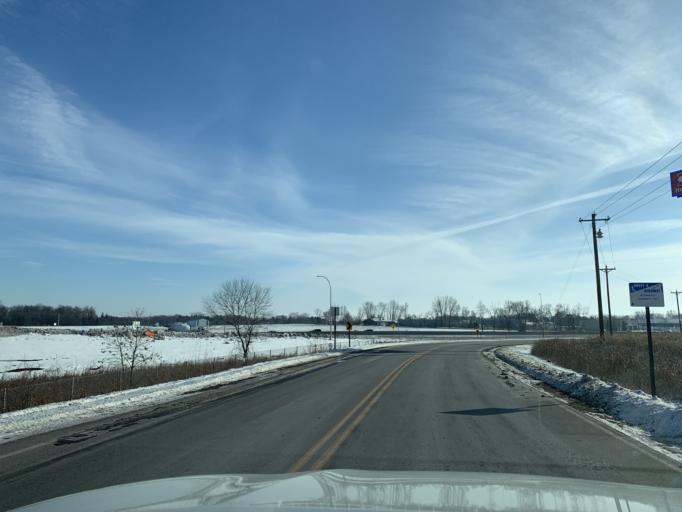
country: US
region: Minnesota
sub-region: Anoka County
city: Columbus
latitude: 45.2499
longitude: -93.0269
